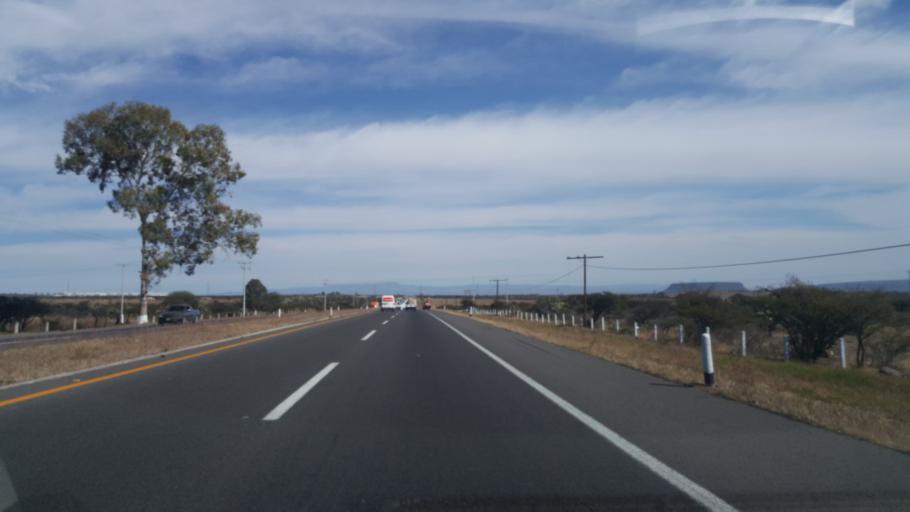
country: MX
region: Jalisco
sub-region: Lagos de Moreno
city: Cristeros [Fraccionamiento]
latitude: 21.3028
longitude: -102.1038
